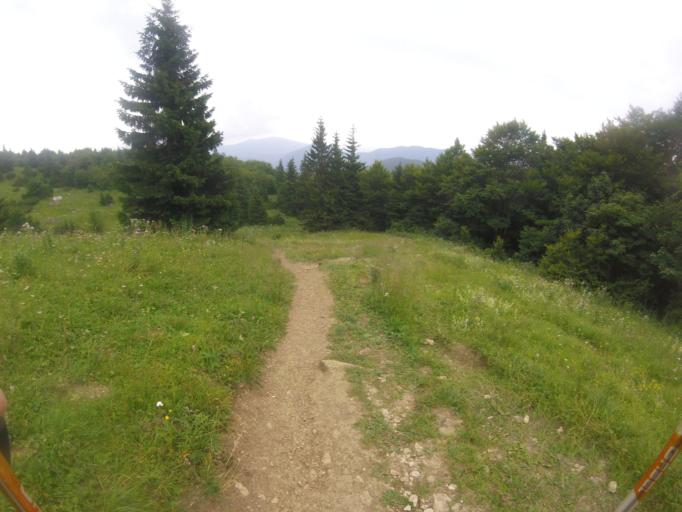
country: SK
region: Zilinsky
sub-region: Okres Zilina
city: Terchova
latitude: 49.2289
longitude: 19.1039
